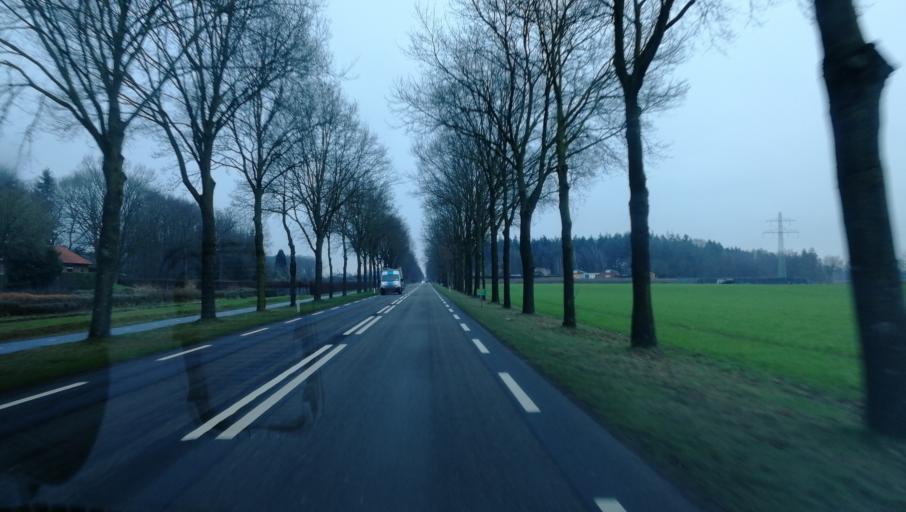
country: NL
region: Limburg
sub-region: Gemeente Beesel
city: Reuver
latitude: 51.3168
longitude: 6.0753
